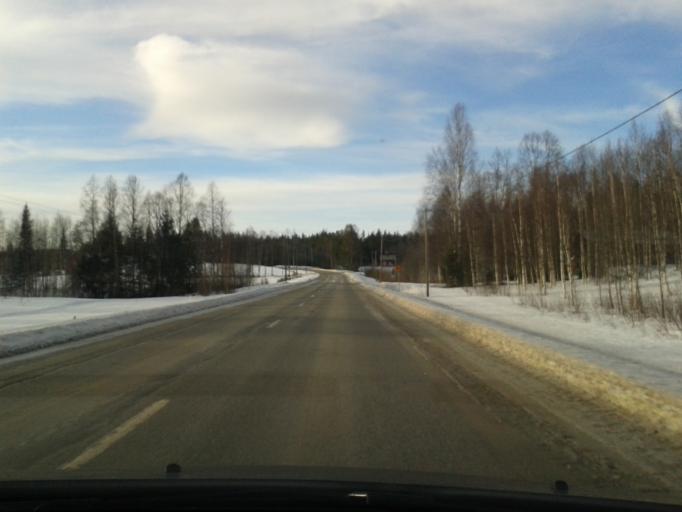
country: SE
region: Vaesternorrland
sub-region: OErnskoeldsviks Kommun
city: Bredbyn
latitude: 63.5292
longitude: 17.9878
